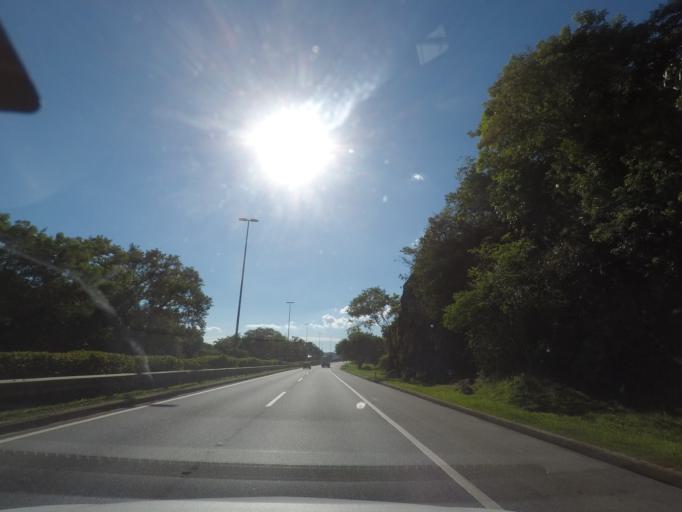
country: BR
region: Rio de Janeiro
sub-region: Sao Goncalo
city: Sao Goncalo
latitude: -22.6656
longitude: -43.1016
